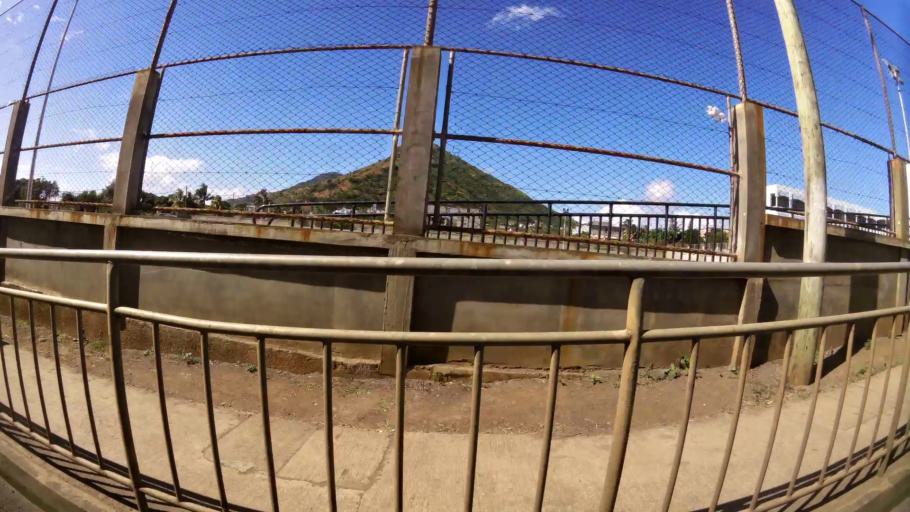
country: MU
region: Black River
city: Cascavelle
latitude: -20.2646
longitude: 57.4166
